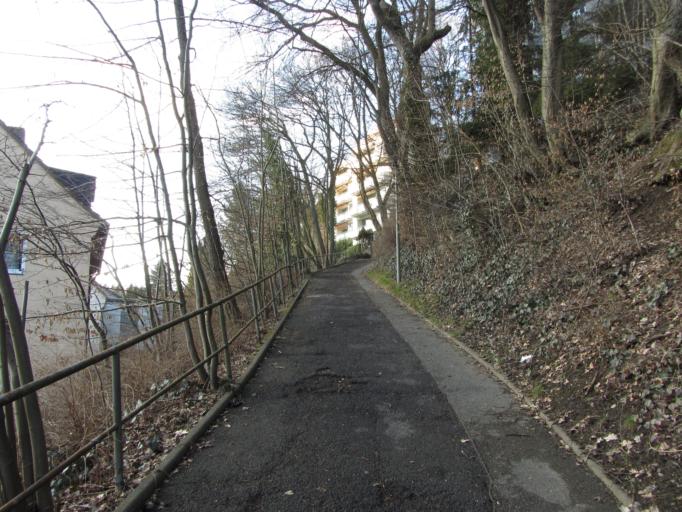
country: DE
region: North Rhine-Westphalia
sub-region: Regierungsbezirk Arnsberg
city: Siegen
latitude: 50.8801
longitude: 8.0138
